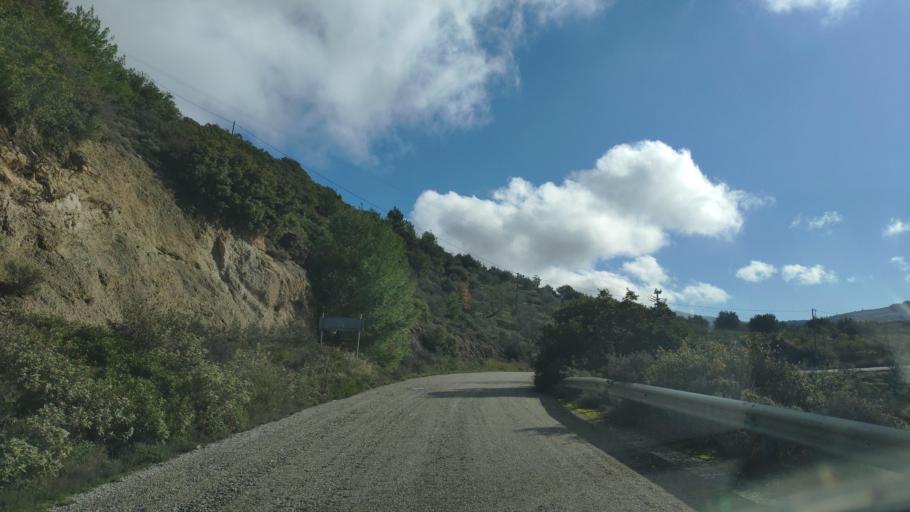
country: GR
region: West Greece
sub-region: Nomos Achaias
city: Aiyira
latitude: 38.0965
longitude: 22.4390
